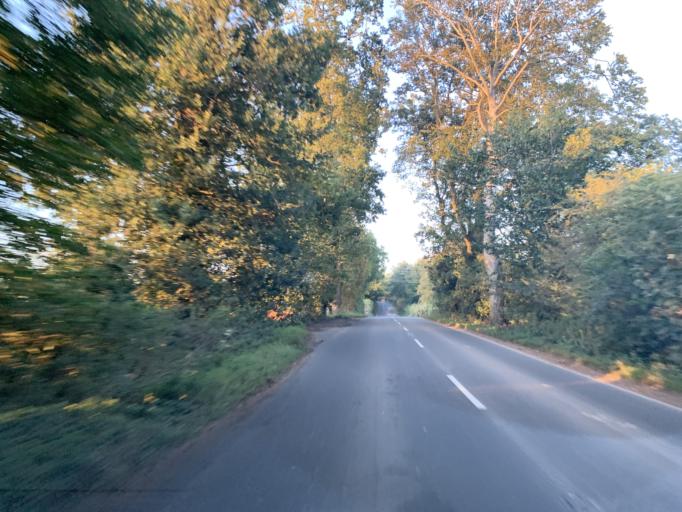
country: GB
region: England
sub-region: Wiltshire
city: Wilton
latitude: 51.0945
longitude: -1.8443
